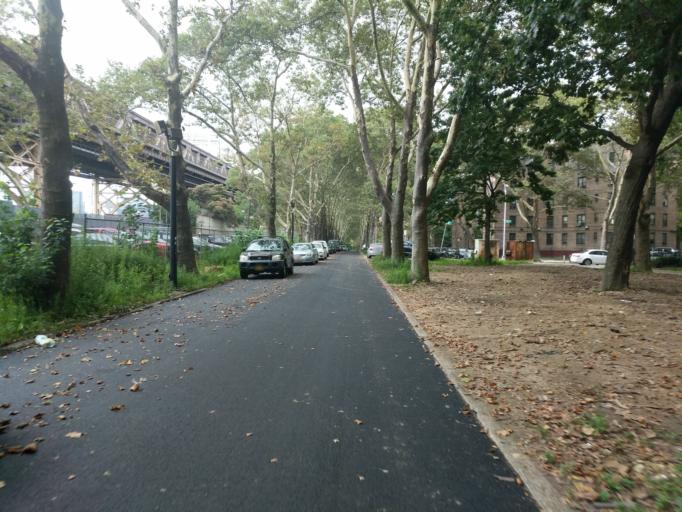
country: US
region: New York
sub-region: Queens County
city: Long Island City
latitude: 40.7531
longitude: -73.9447
